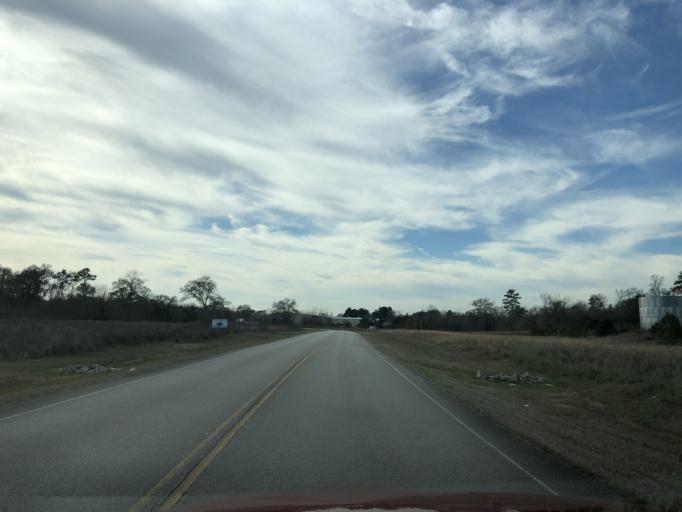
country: US
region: Texas
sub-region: Montgomery County
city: Magnolia
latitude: 30.4020
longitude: -95.6935
